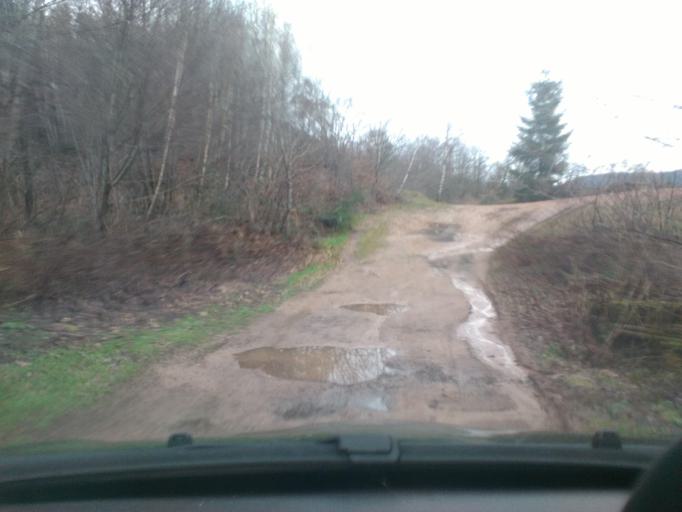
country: FR
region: Lorraine
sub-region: Departement des Vosges
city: Senones
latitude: 48.4102
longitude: 6.9791
